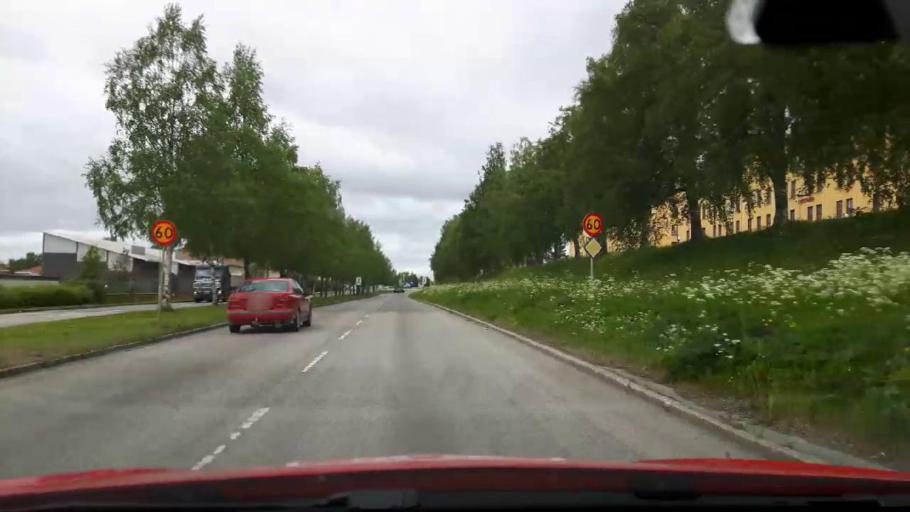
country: SE
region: Jaemtland
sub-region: OEstersunds Kommun
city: Ostersund
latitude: 63.1832
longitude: 14.6397
